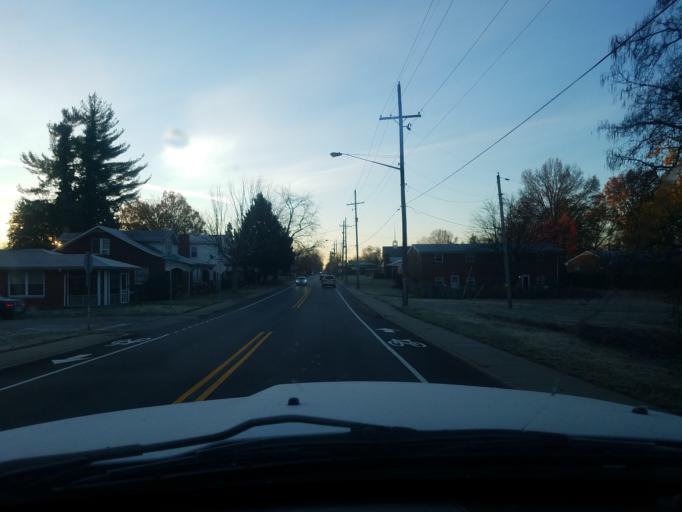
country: US
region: Indiana
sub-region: Floyd County
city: New Albany
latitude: 38.3058
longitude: -85.8083
